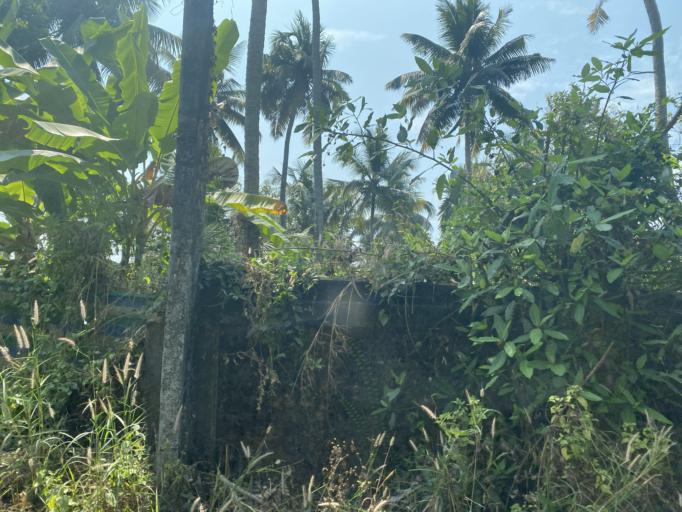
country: IN
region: Kerala
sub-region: Ernakulam
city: Elur
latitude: 10.1080
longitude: 76.2299
